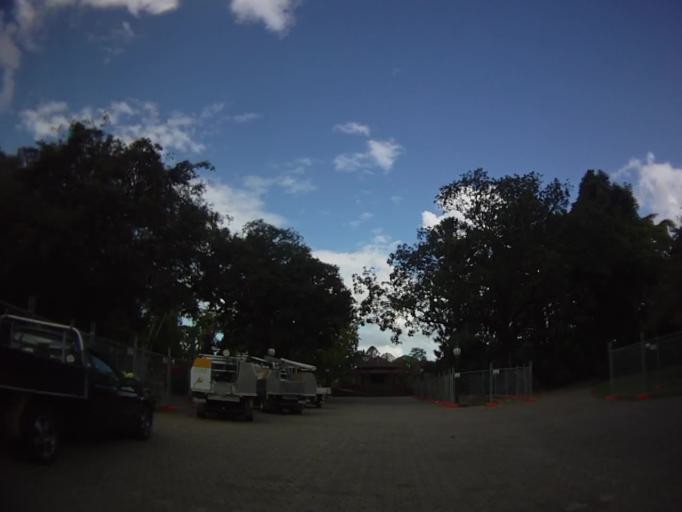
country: AU
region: Queensland
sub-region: Brisbane
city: Brisbane
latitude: -27.4739
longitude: 153.0294
